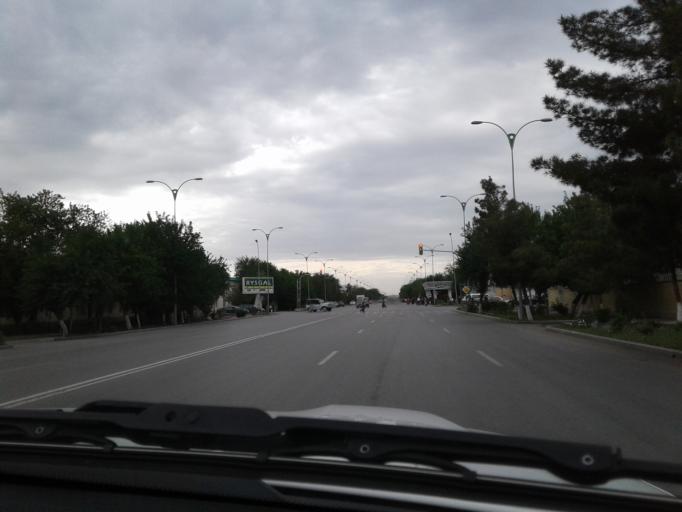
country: TM
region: Mary
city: Mary
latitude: 37.5900
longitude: 61.8342
